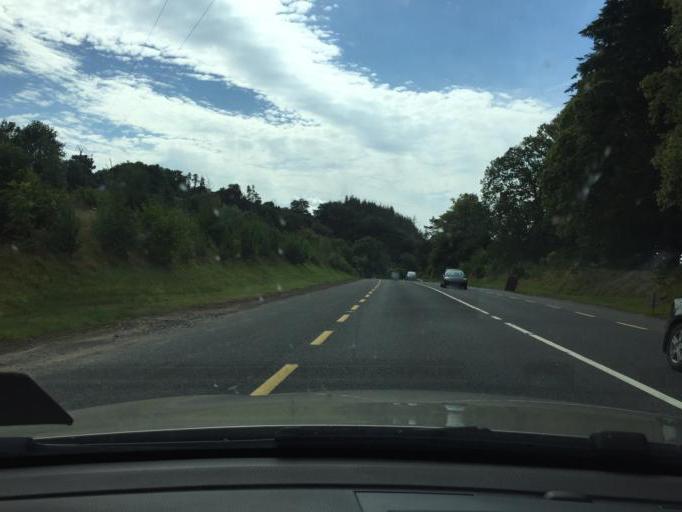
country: IE
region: Leinster
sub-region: Kilkenny
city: Mooncoin
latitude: 52.2388
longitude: -7.2595
